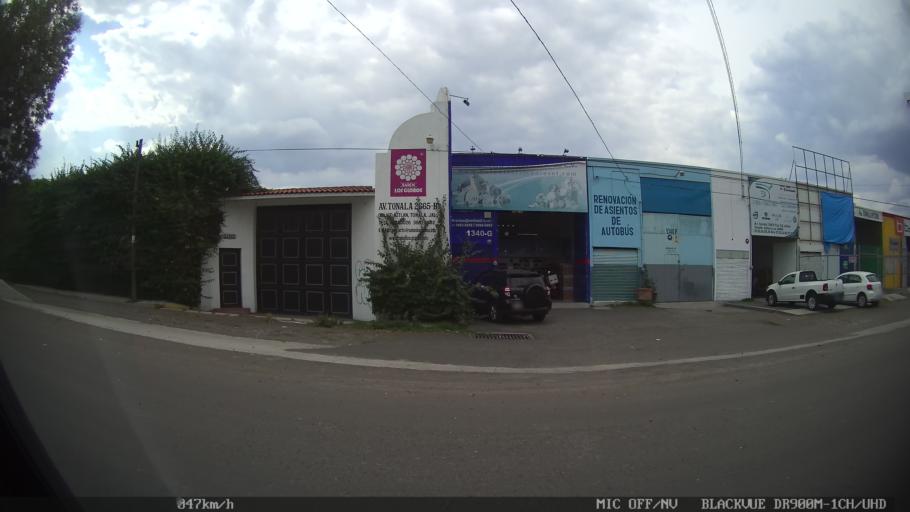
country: MX
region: Jalisco
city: Tlaquepaque
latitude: 20.6170
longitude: -103.2763
